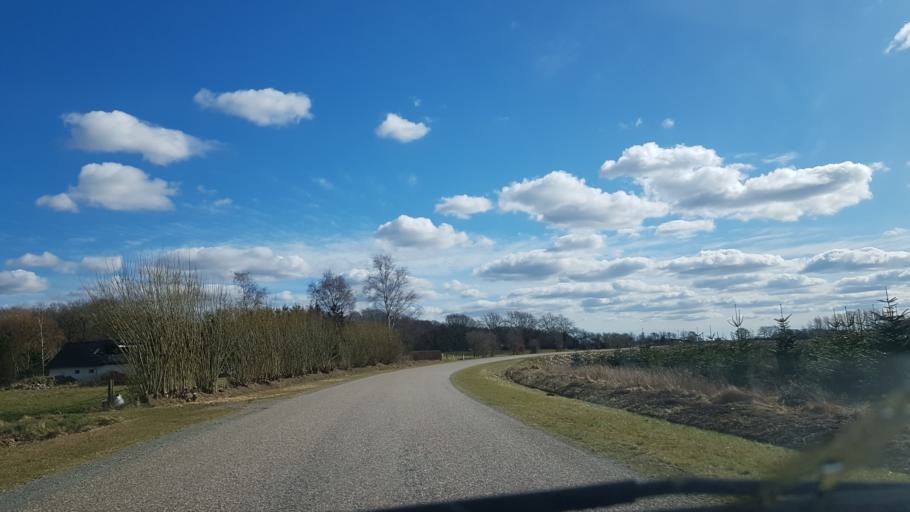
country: DK
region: South Denmark
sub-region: Vejen Kommune
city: Vejen
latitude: 55.4204
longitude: 9.1805
